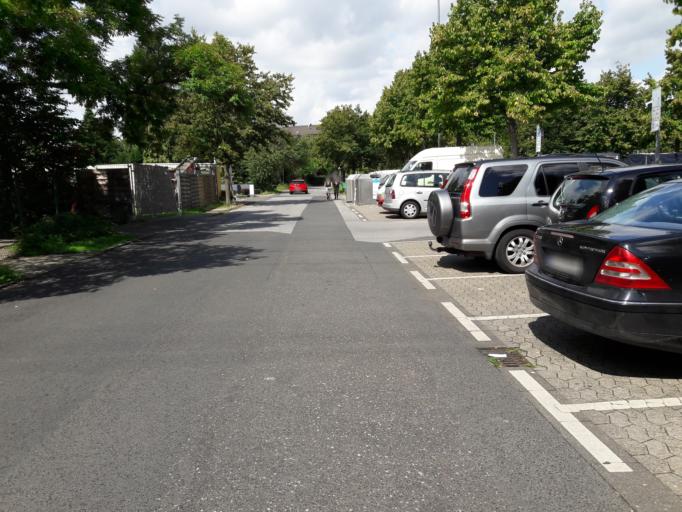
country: DE
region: North Rhine-Westphalia
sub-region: Regierungsbezirk Dusseldorf
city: Dusseldorf
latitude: 51.2024
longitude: 6.8377
